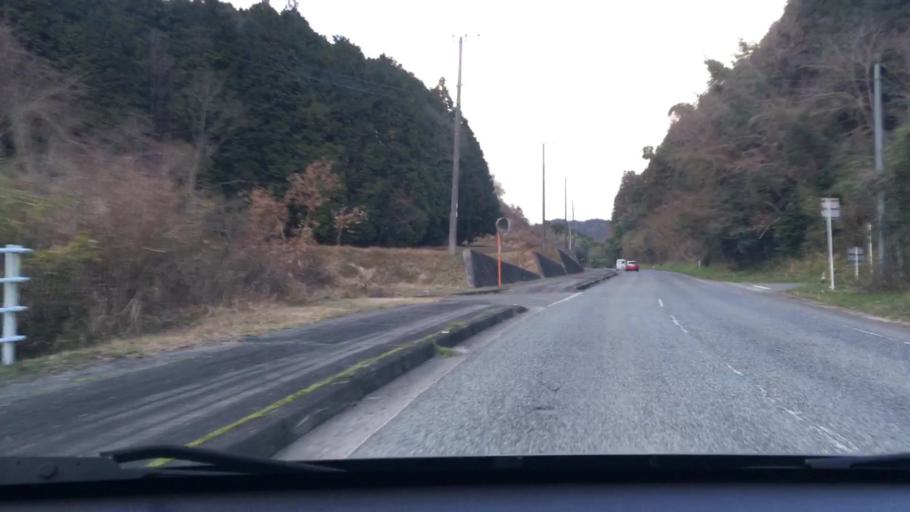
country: JP
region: Oita
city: Bungo-Takada-shi
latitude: 33.4739
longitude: 131.3843
